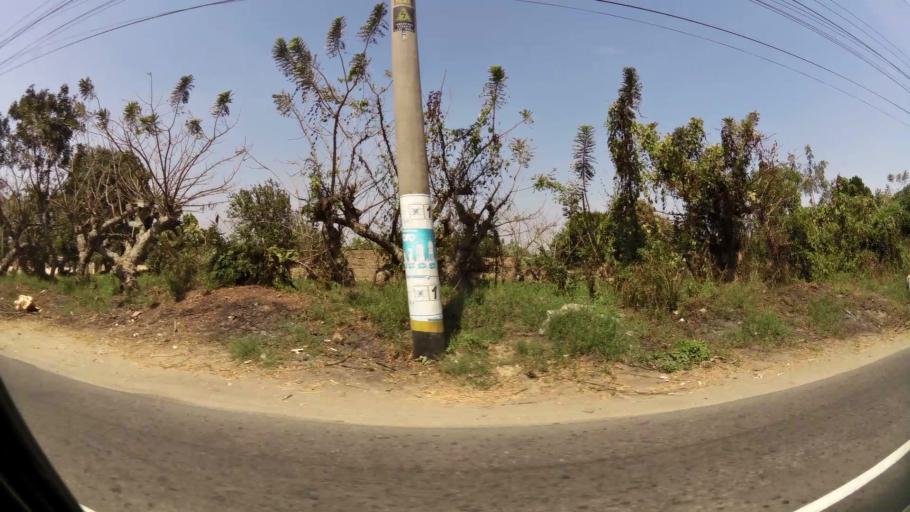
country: PE
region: La Libertad
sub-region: Chepen
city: Chepen
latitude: -7.2251
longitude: -79.4418
